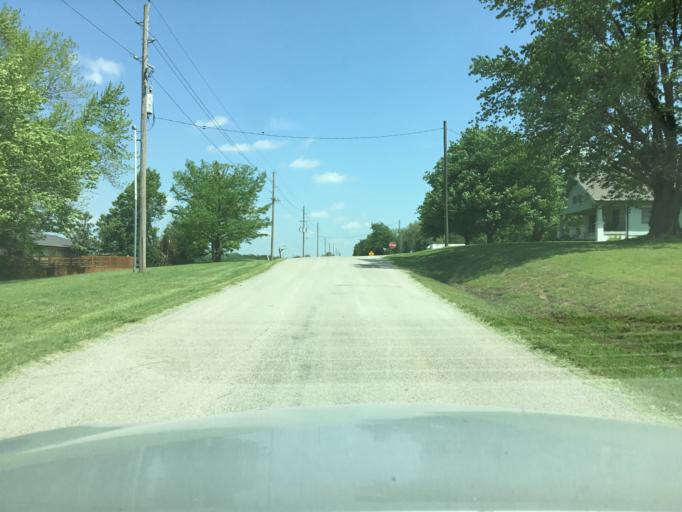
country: US
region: Kansas
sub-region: Labette County
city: Parsons
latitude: 37.3546
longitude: -95.2495
